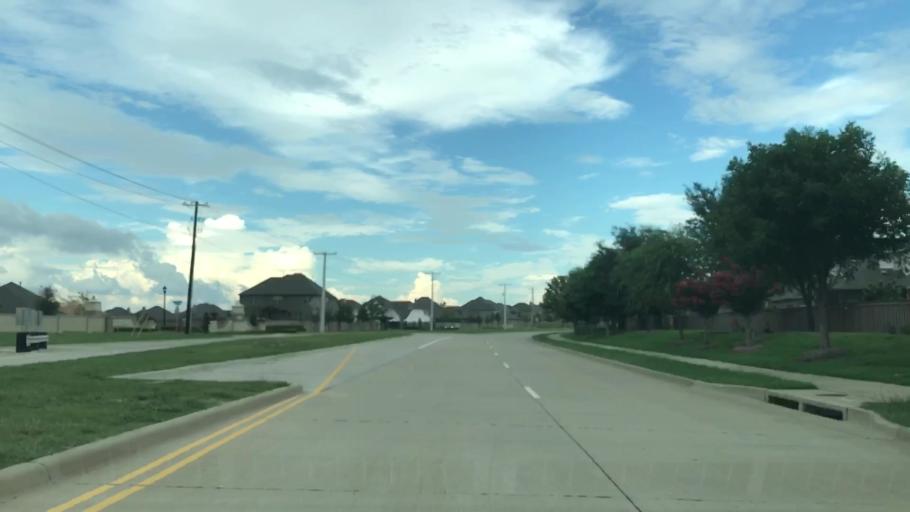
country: US
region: Texas
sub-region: Collin County
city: Prosper
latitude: 33.1885
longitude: -96.7791
